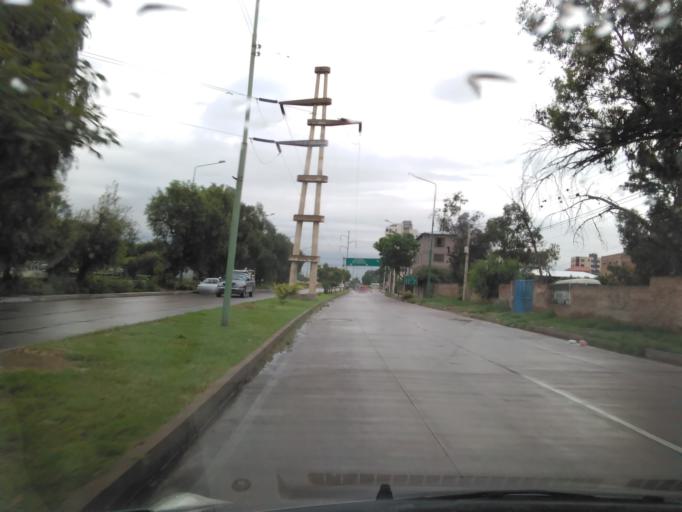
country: BO
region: Cochabamba
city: Cochabamba
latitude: -17.3762
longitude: -66.1401
